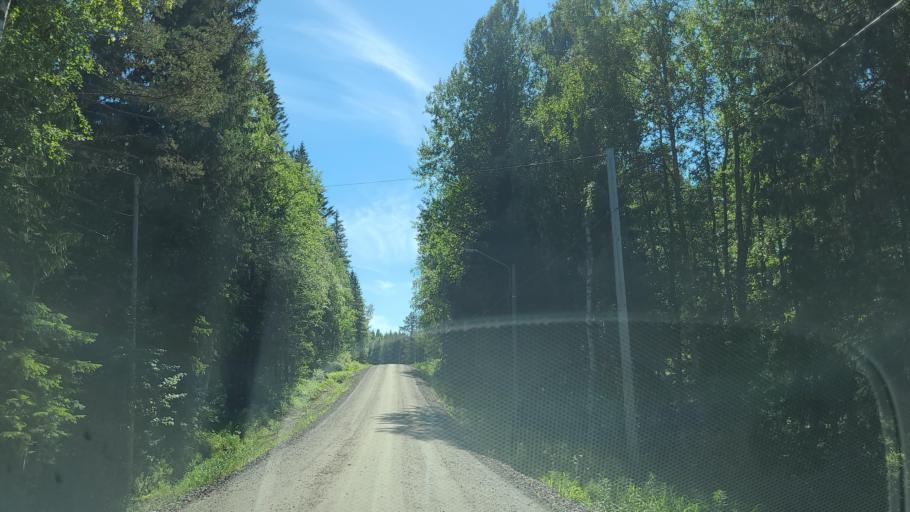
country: SE
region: Vaesterbotten
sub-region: Bjurholms Kommun
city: Bjurholm
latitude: 63.6621
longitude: 19.0786
